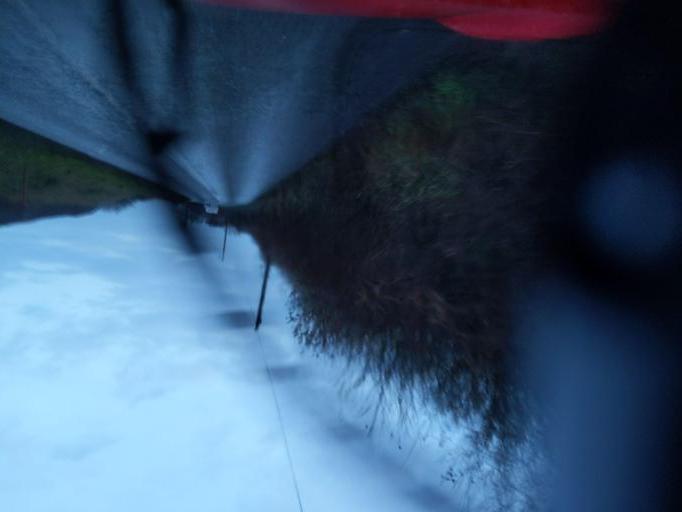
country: GB
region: England
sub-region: Devon
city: Wembury
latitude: 50.3432
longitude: -4.0755
